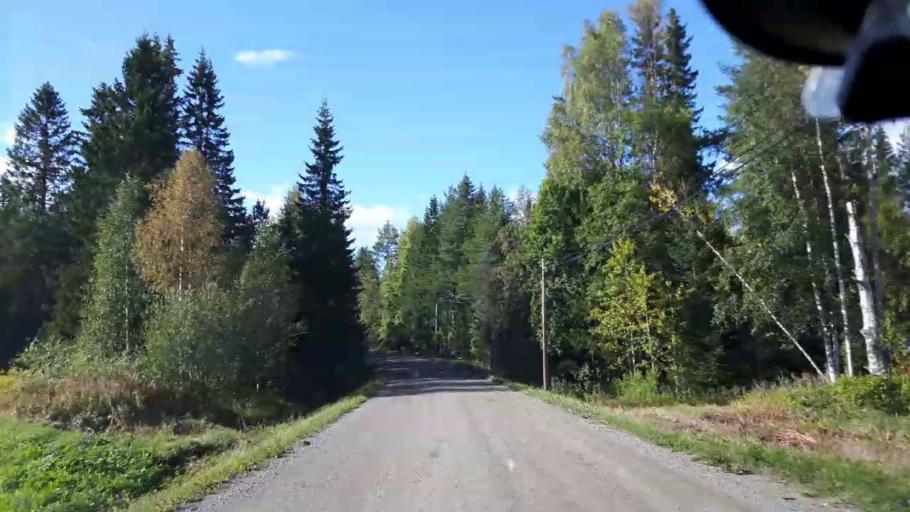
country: SE
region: Vaesternorrland
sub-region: Solleftea Kommun
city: As
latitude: 63.4614
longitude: 16.2539
